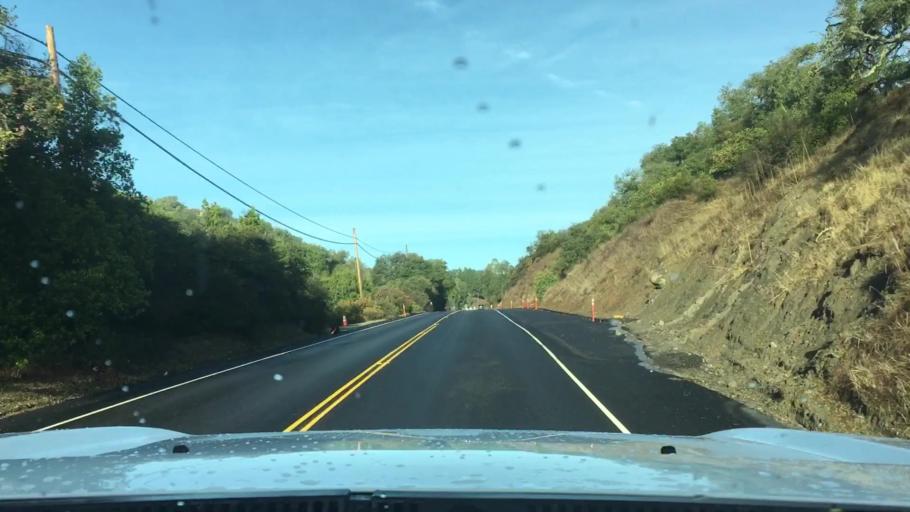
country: US
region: California
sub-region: San Luis Obispo County
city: Atascadero
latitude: 35.4526
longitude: -120.7099
